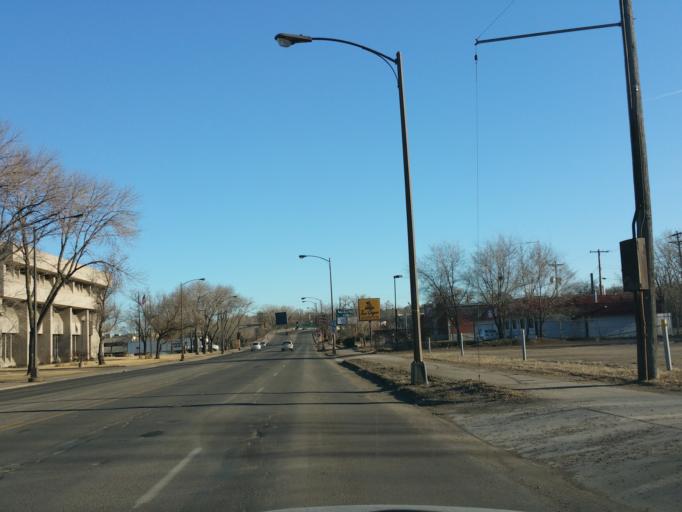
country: US
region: Minnesota
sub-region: Ramsey County
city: Saint Paul
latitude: 44.9400
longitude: -93.0838
